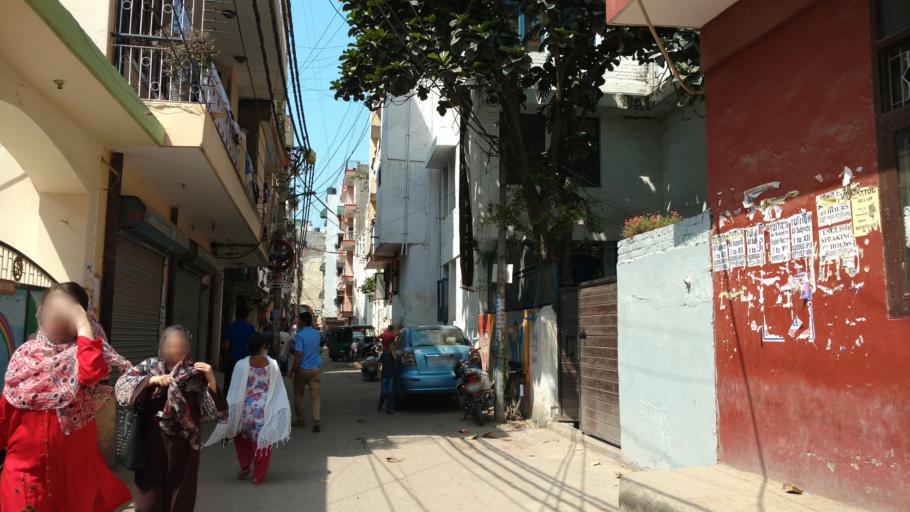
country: IN
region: NCT
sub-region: New Delhi
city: New Delhi
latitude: 28.5310
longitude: 77.2181
